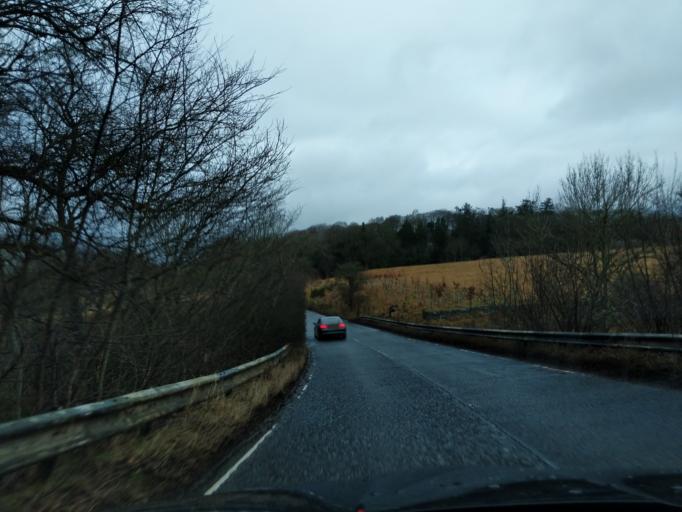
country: GB
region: Scotland
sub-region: The Scottish Borders
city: Galashiels
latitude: 55.6432
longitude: -2.8481
